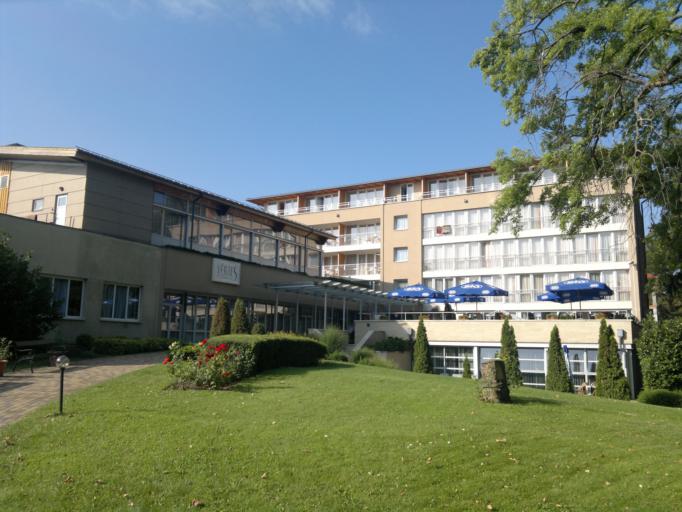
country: HU
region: Somogy
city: Siofok
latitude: 46.9105
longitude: 18.0499
